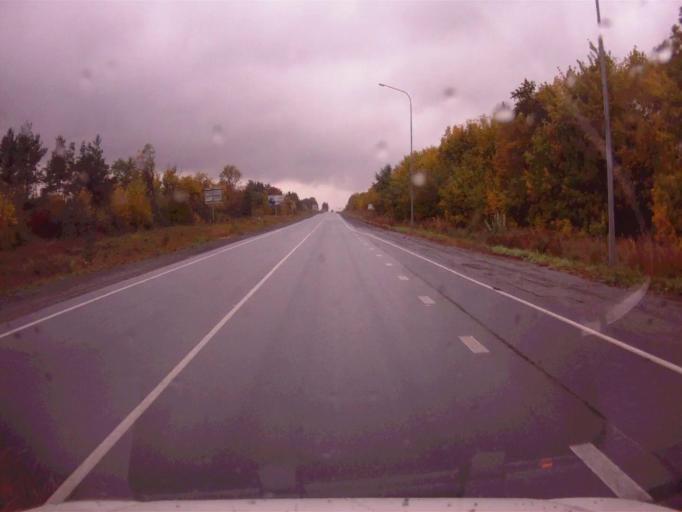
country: RU
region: Chelyabinsk
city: Roshchino
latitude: 55.3699
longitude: 61.1771
